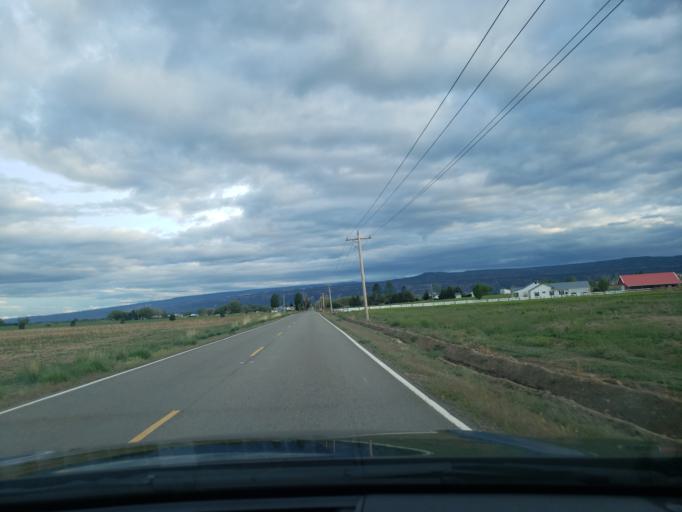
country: US
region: Colorado
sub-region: Mesa County
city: Fruita
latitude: 39.2145
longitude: -108.7011
